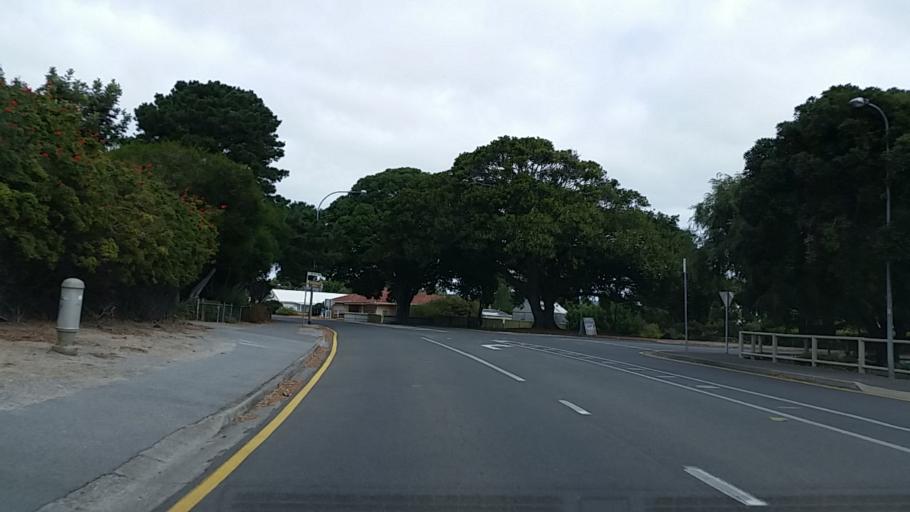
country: AU
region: South Australia
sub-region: Yankalilla
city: Normanville
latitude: -35.4444
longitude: 138.3162
